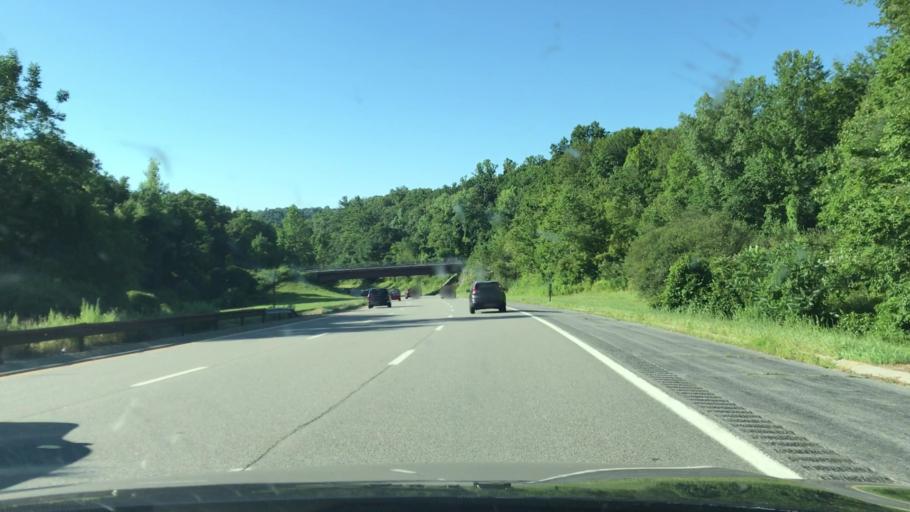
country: US
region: New York
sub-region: Westchester County
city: Yorktown Heights
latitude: 41.2261
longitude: -73.8071
